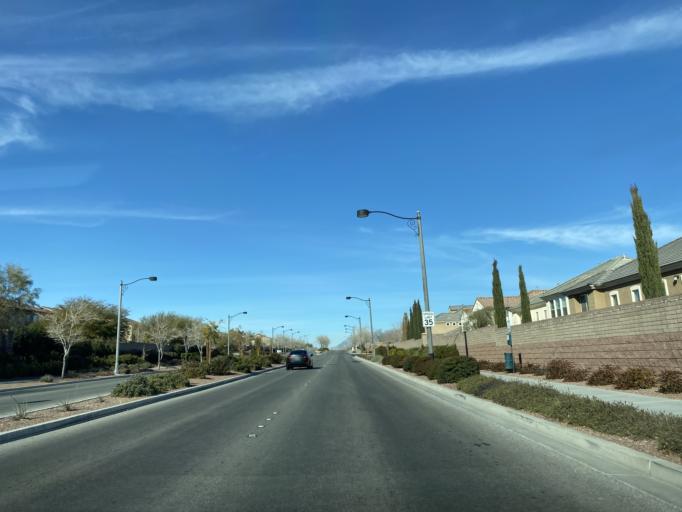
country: US
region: Nevada
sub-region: Clark County
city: Summerlin South
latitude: 36.2890
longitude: -115.3195
